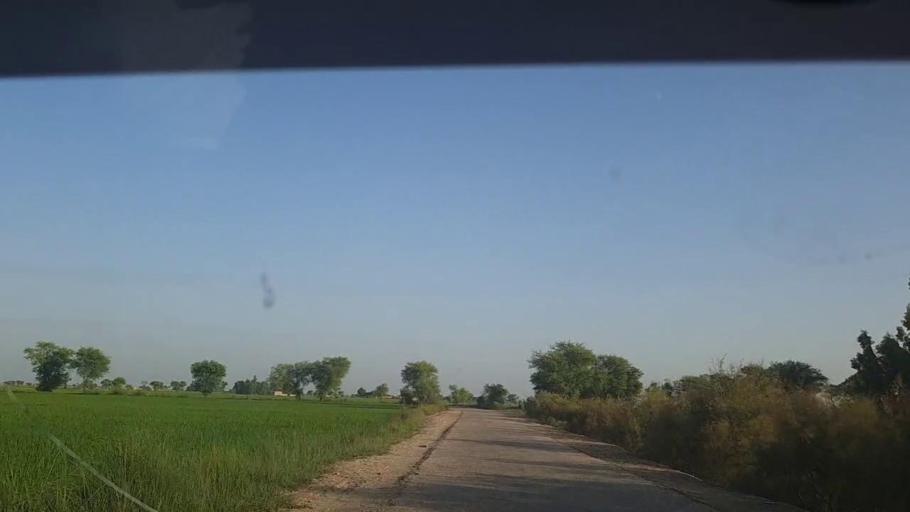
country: PK
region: Sindh
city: Thul
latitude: 28.2048
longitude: 68.8725
